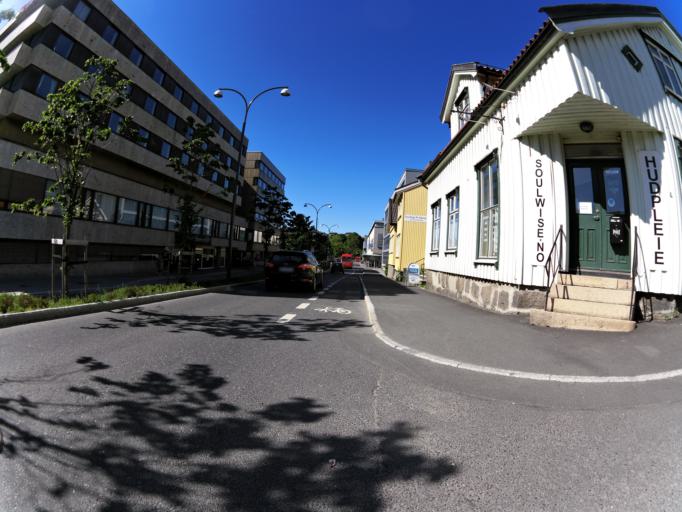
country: NO
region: Ostfold
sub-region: Fredrikstad
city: Fredrikstad
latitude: 59.2128
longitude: 10.9395
